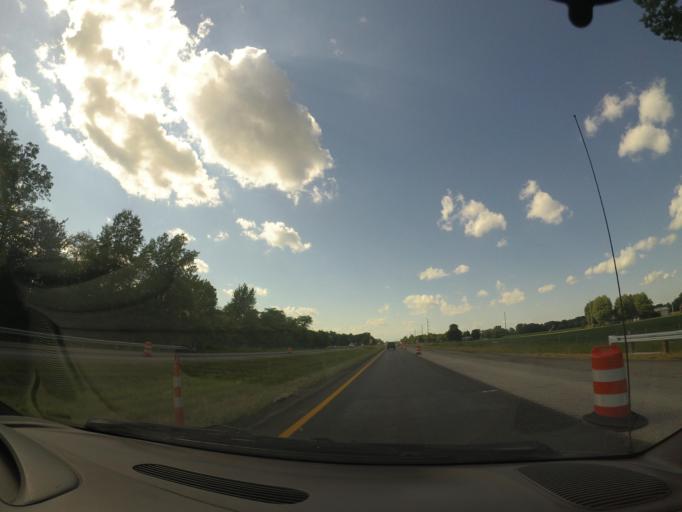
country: US
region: Ohio
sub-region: Sandusky County
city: Fremont
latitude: 41.3395
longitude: -83.0639
